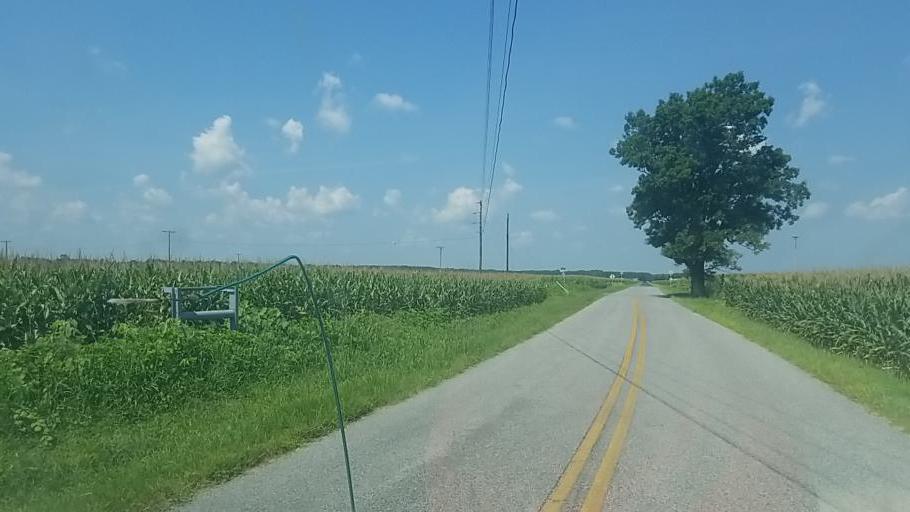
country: US
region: Maryland
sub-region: Worcester County
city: Berlin
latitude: 38.2936
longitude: -75.2491
